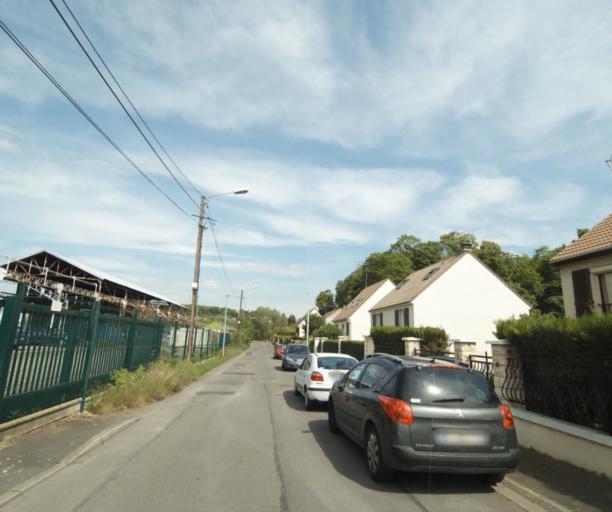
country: FR
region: Ile-de-France
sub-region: Departement des Yvelines
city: Les Mureaux
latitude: 48.9962
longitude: 1.9013
